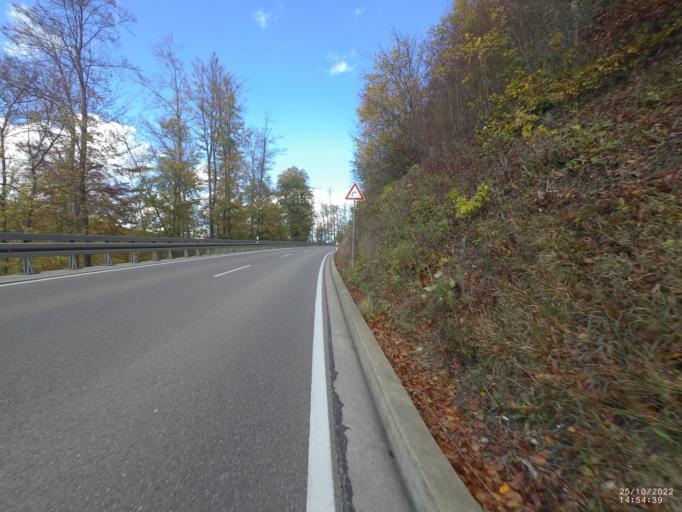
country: DE
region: Baden-Wuerttemberg
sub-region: Regierungsbezirk Stuttgart
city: Bohmenkirch
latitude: 48.6645
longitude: 9.8976
